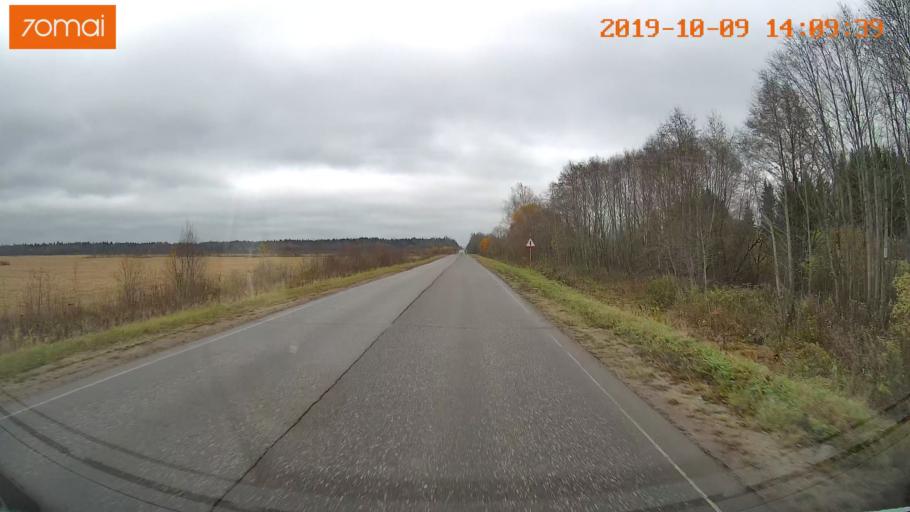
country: RU
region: Kostroma
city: Buy
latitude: 58.4812
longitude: 41.4571
